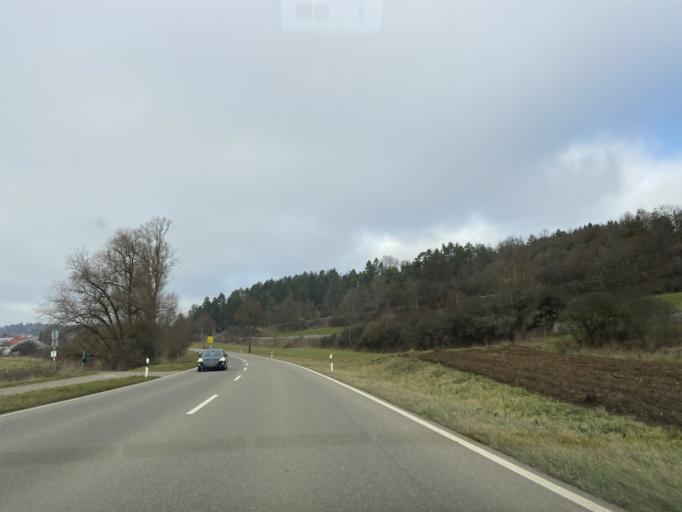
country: DE
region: Baden-Wuerttemberg
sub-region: Tuebingen Region
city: Gammertingen
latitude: 48.2414
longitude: 9.2260
